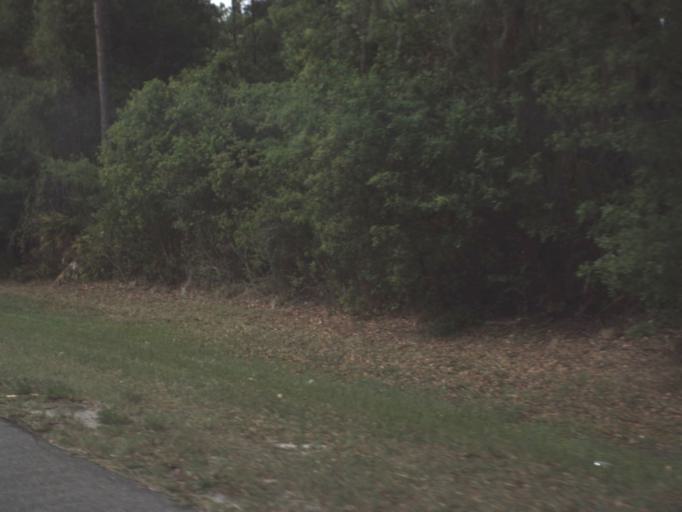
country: US
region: Florida
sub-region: Putnam County
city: Crescent City
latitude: 29.5053
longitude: -81.4908
